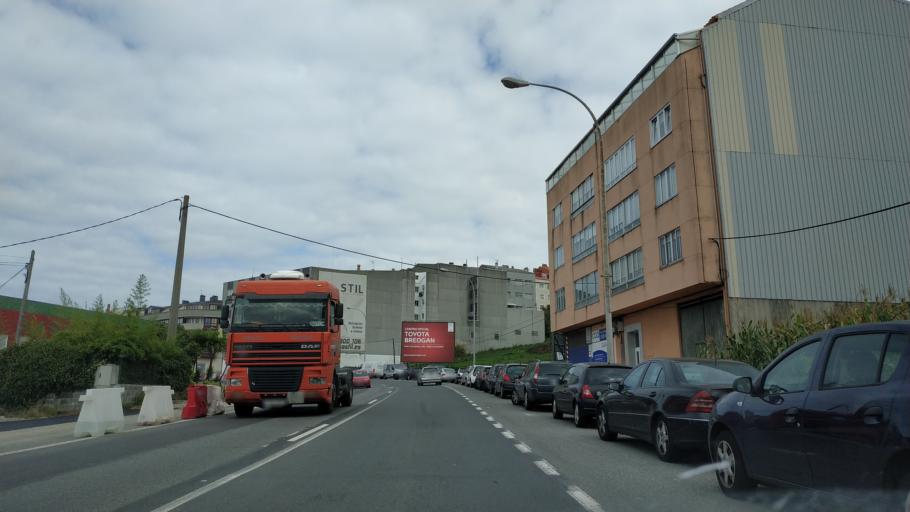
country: ES
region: Galicia
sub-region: Provincia da Coruna
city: Arteixo
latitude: 43.3109
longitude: -8.5015
